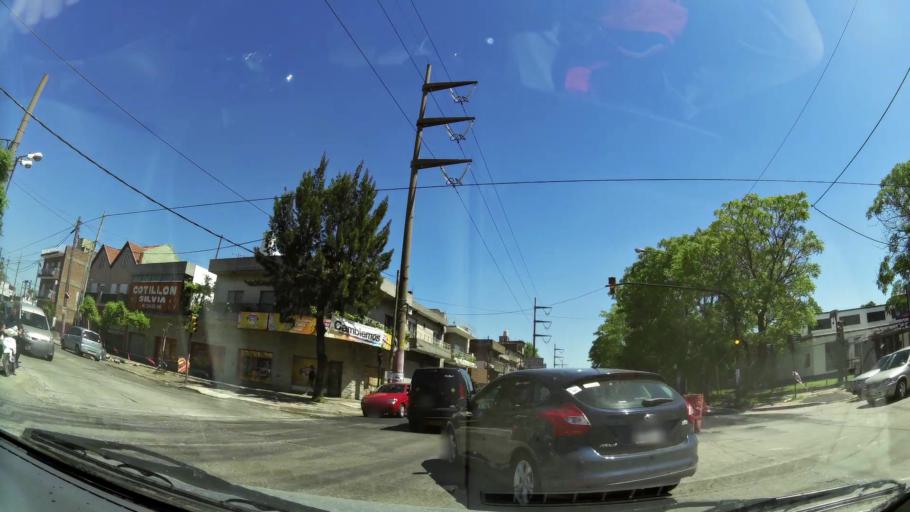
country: AR
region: Buenos Aires
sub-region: Partido de Quilmes
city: Quilmes
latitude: -34.7298
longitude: -58.2826
